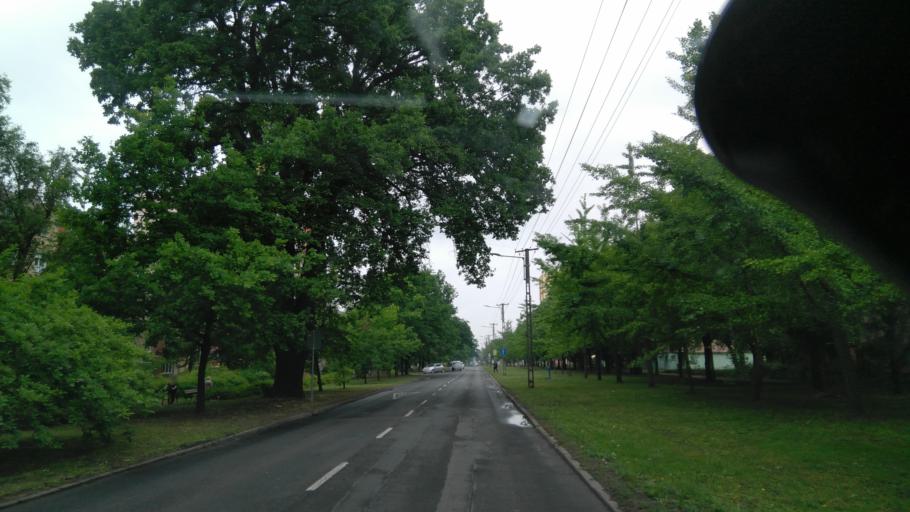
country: HU
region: Bekes
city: Bekescsaba
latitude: 46.6668
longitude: 21.1183
